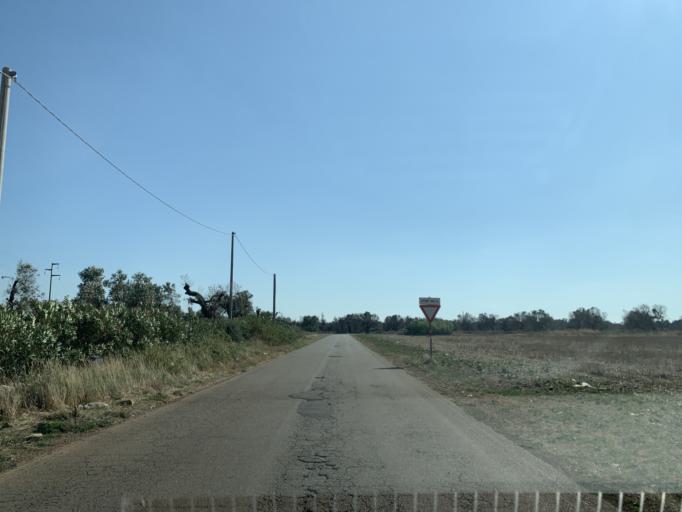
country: IT
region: Apulia
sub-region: Provincia di Lecce
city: Copertino
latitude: 40.2596
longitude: 18.0222
